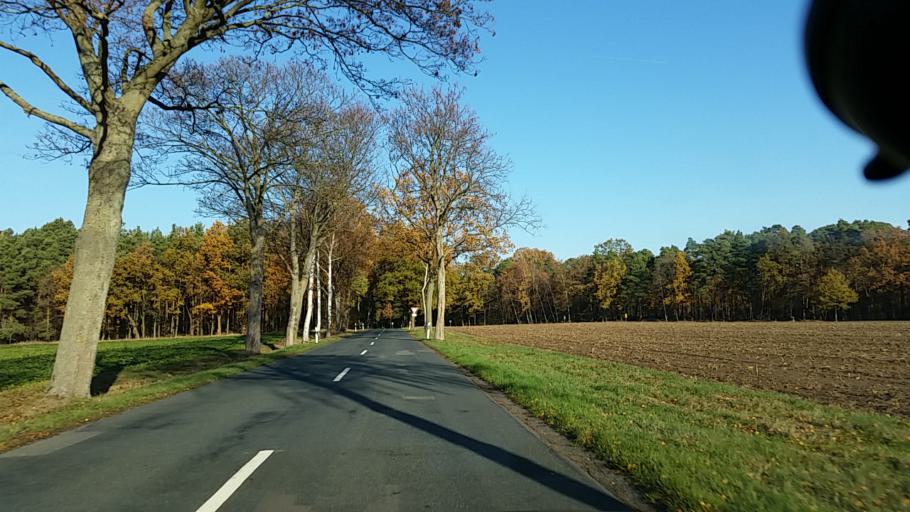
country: DE
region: Lower Saxony
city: Tulau
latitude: 52.6322
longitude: 10.8762
